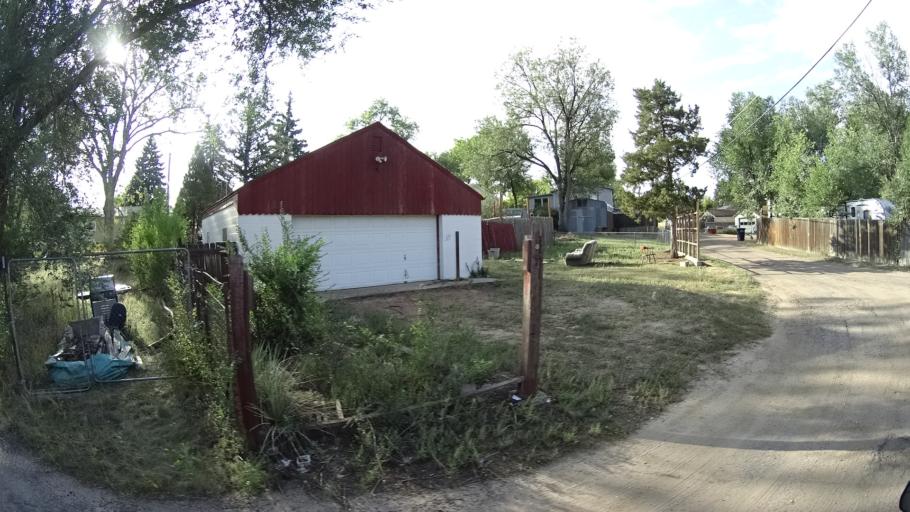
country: US
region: Colorado
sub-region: El Paso County
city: Colorado Springs
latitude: 38.8563
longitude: -104.7717
